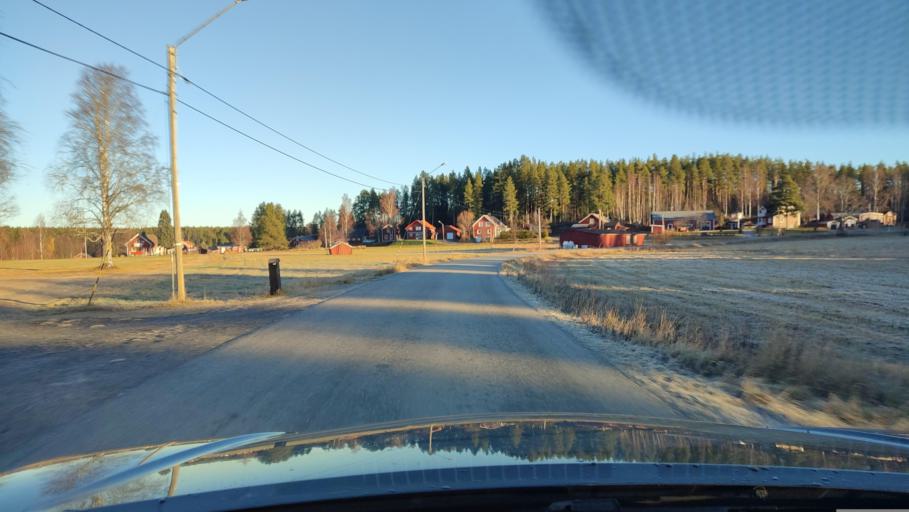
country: SE
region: Vaesterbotten
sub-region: Skelleftea Kommun
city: Soedra Bergsbyn
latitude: 64.6323
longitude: 21.0619
